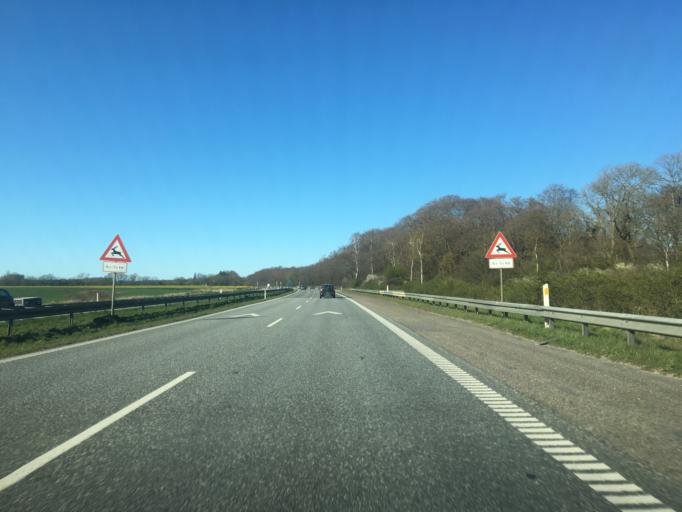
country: DK
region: Zealand
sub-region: Koge Kommune
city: Bjaeverskov
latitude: 55.4040
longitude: 12.0991
